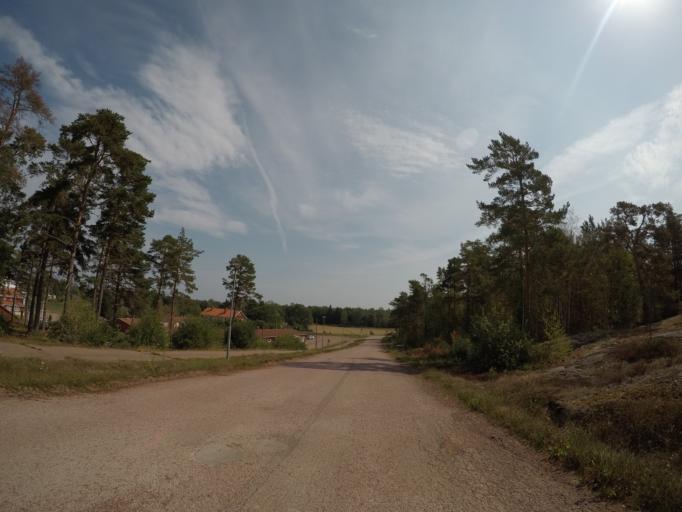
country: AX
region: Alands landsbygd
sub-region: Finstroem
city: Finstroem
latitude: 60.2232
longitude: 19.9783
